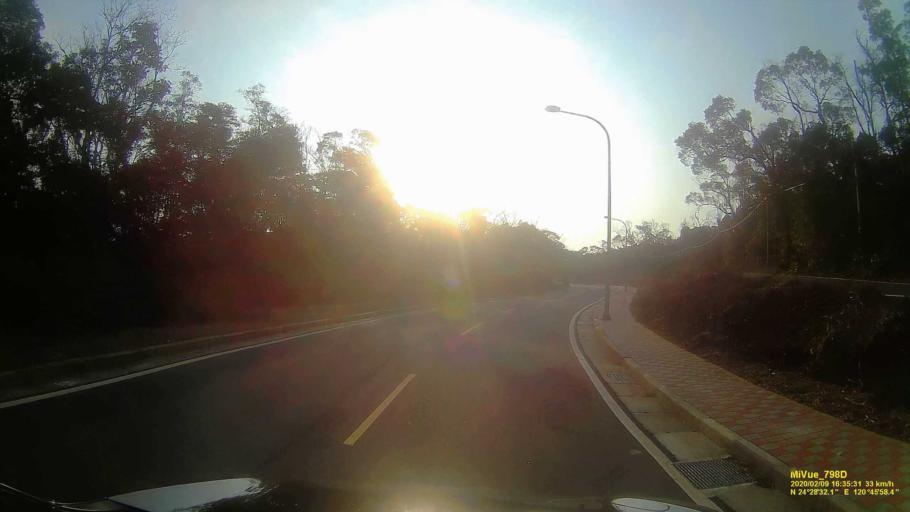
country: TW
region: Taiwan
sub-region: Miaoli
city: Miaoli
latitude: 24.4755
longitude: 120.7660
